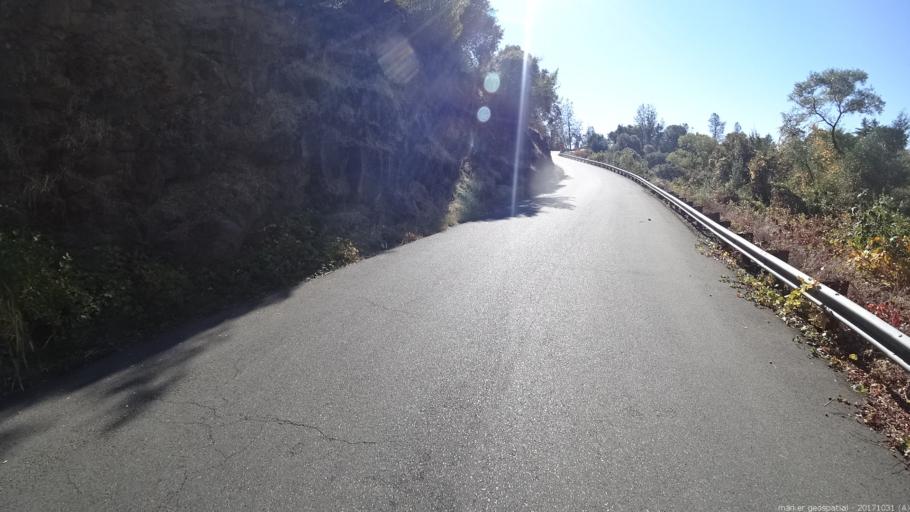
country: US
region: California
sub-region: Shasta County
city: Shingletown
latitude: 40.4469
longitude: -121.8680
